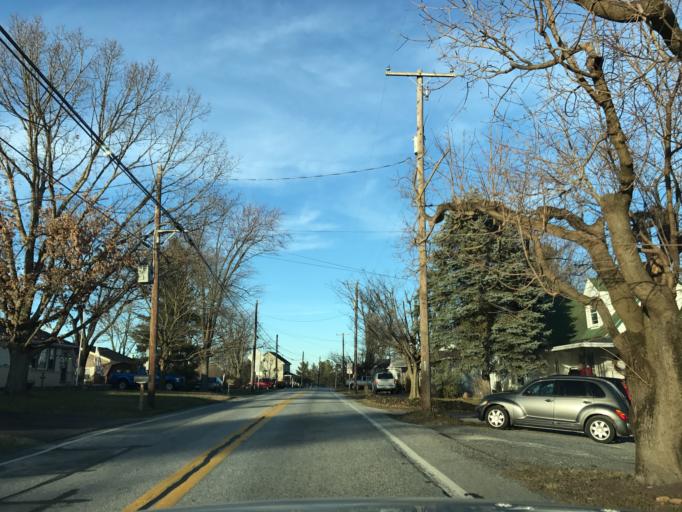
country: US
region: Pennsylvania
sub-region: Lancaster County
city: Elizabethtown
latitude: 40.1249
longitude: -76.5996
